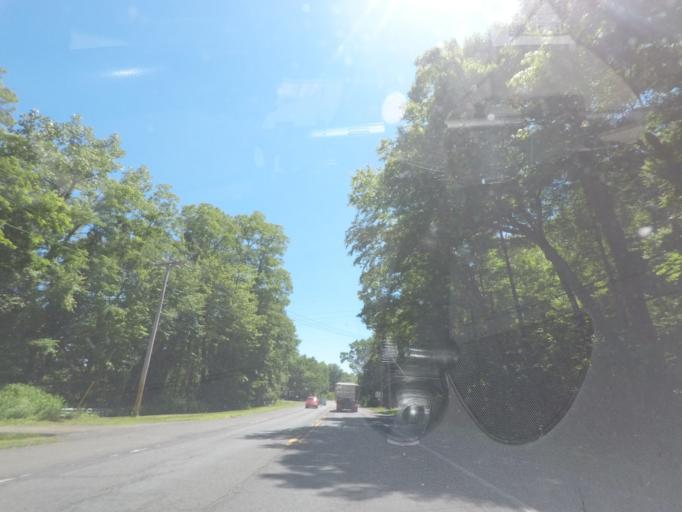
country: US
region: Massachusetts
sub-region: Hampden County
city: Westfield
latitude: 42.1550
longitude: -72.8145
